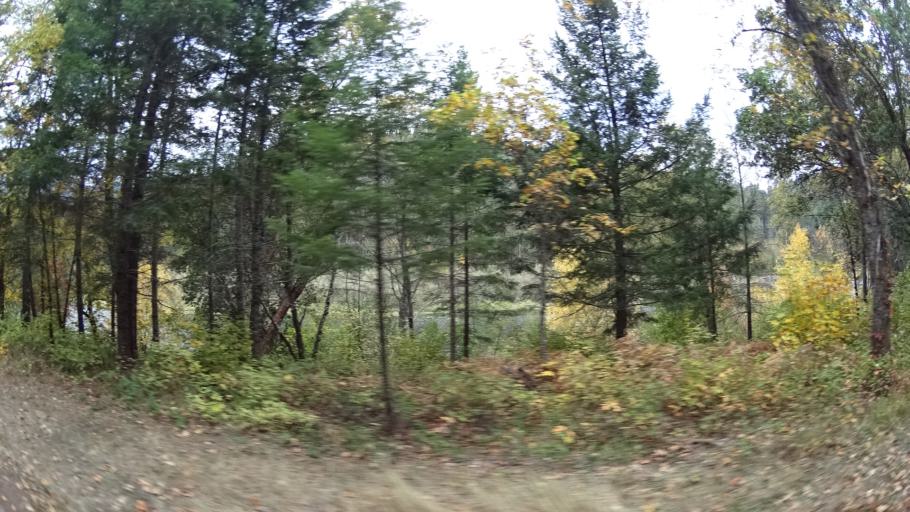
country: US
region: California
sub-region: Siskiyou County
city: Happy Camp
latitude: 41.7767
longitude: -123.3291
